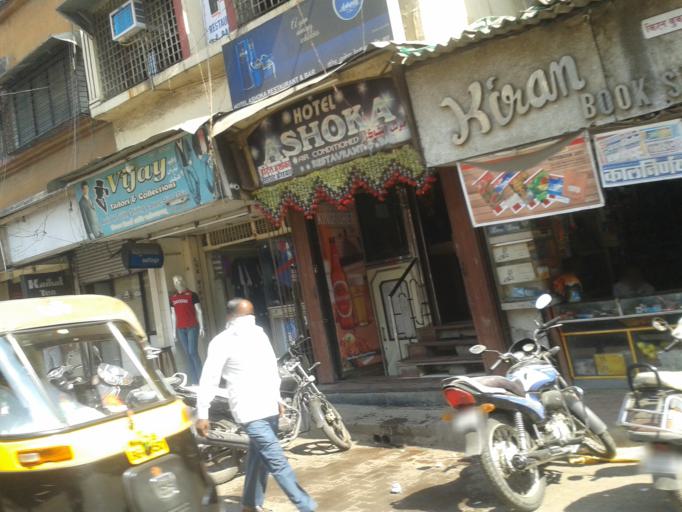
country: IN
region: Maharashtra
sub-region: Thane
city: Ulhasnagar
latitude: 19.2384
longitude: 73.1644
